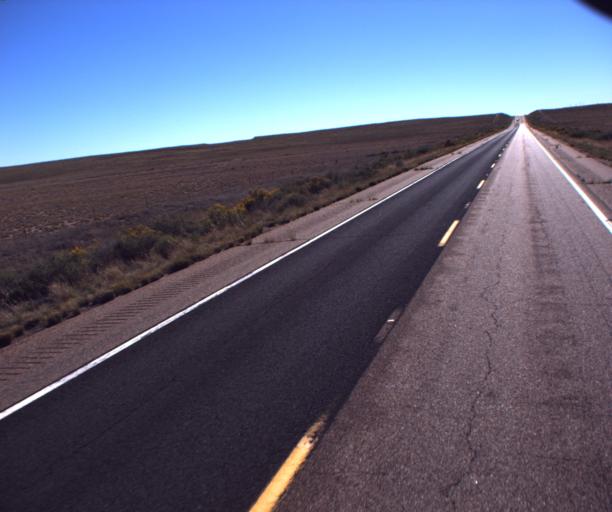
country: US
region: Arizona
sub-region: Navajo County
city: Snowflake
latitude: 34.7586
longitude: -109.8096
